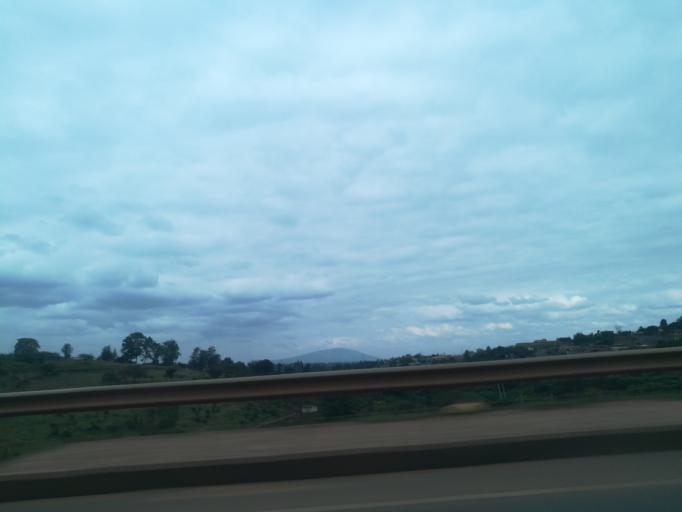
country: KE
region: Nairobi Area
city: Thika
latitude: -1.0621
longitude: 37.0539
